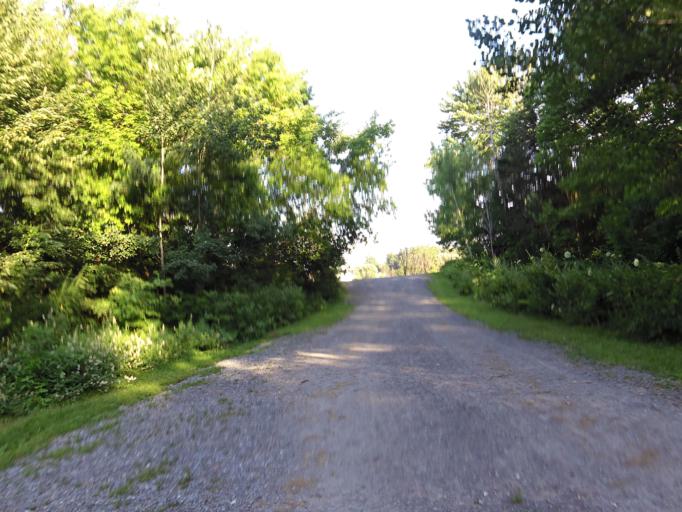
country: CA
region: Ontario
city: Ottawa
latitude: 45.3853
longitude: -75.6897
